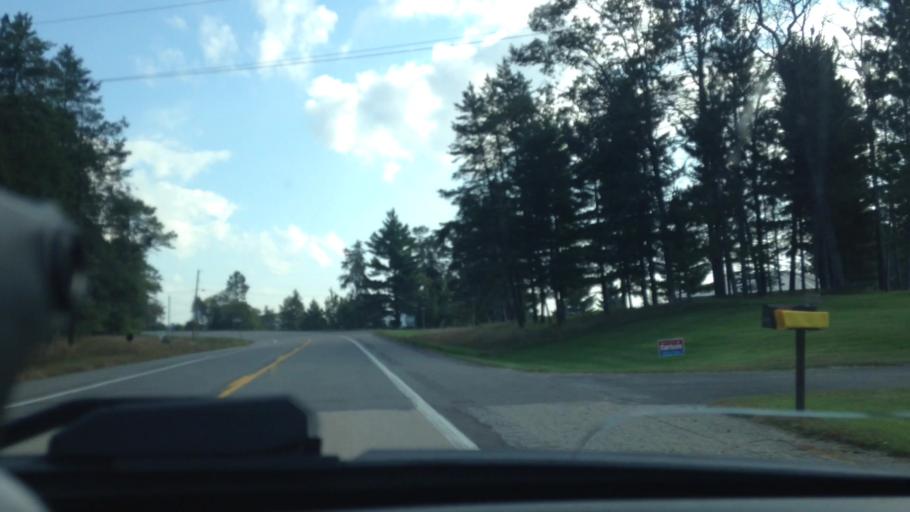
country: US
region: Michigan
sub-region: Dickinson County
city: Norway
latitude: 45.7687
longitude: -87.9116
